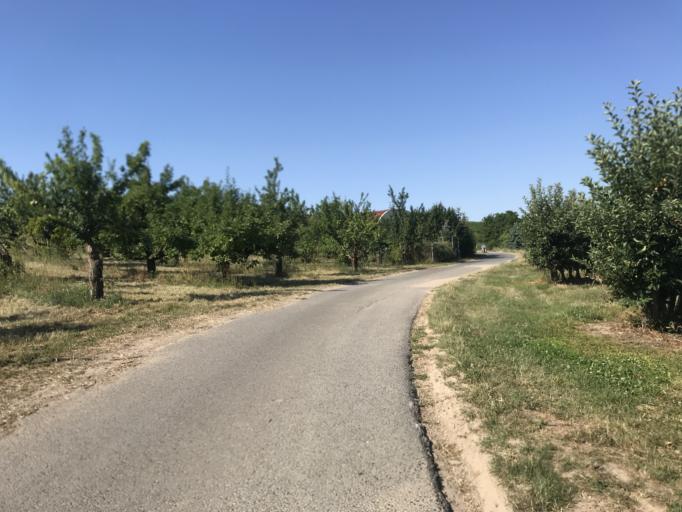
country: DE
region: Rheinland-Pfalz
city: Gau-Algesheim
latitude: 49.9502
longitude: 8.0030
